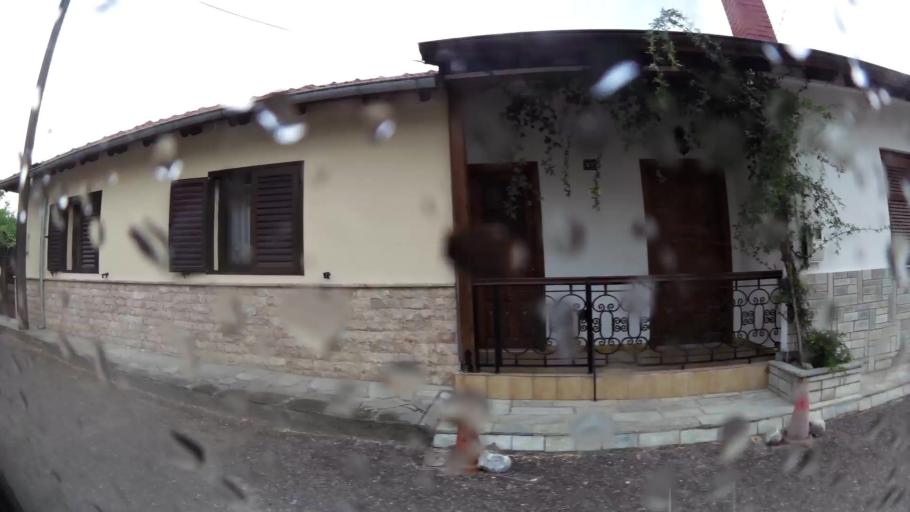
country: GR
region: Central Macedonia
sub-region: Nomos Imathias
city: Veroia
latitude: 40.5269
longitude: 22.2003
